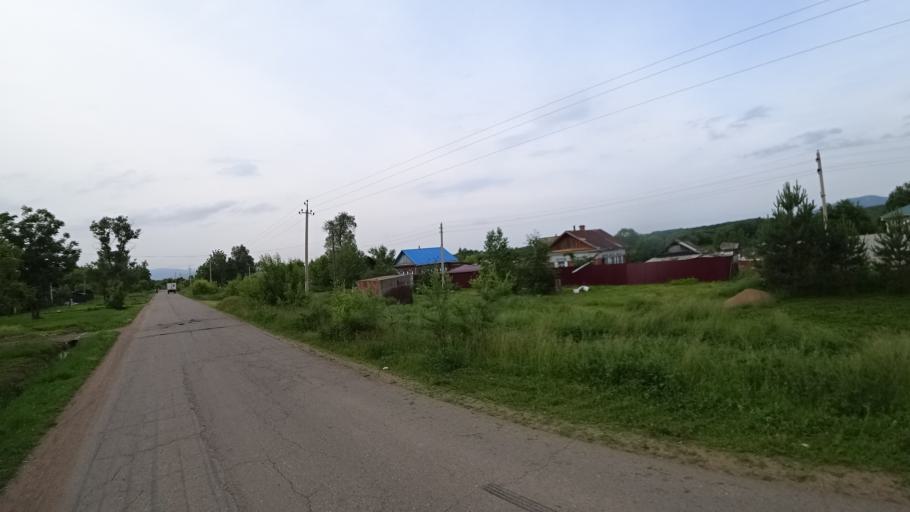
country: RU
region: Primorskiy
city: Novosysoyevka
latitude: 44.2412
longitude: 133.3681
